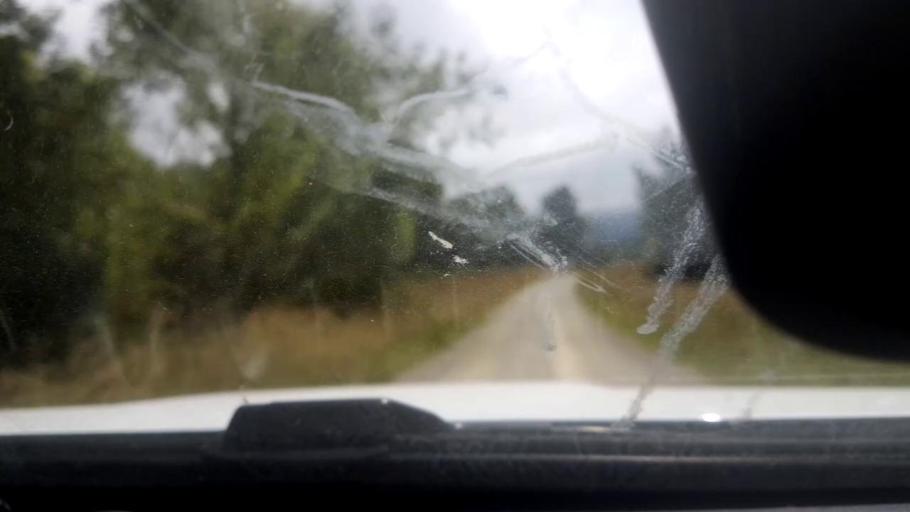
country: NZ
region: Canterbury
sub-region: Timaru District
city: Pleasant Point
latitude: -44.1408
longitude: 171.0832
